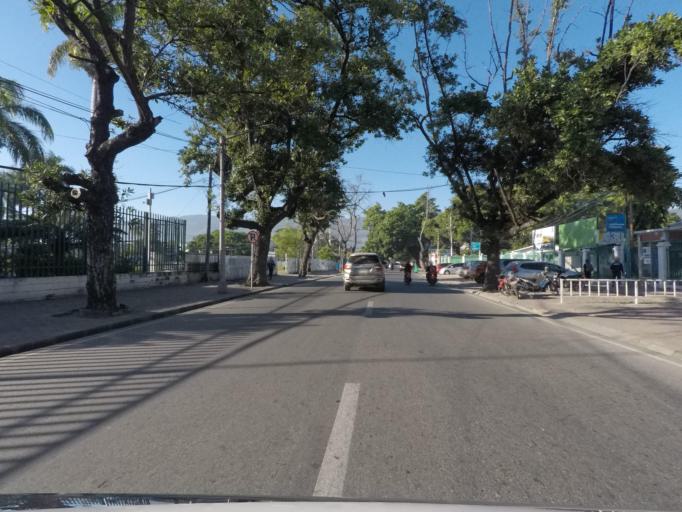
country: TL
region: Dili
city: Dili
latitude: -8.5546
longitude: 125.5797
